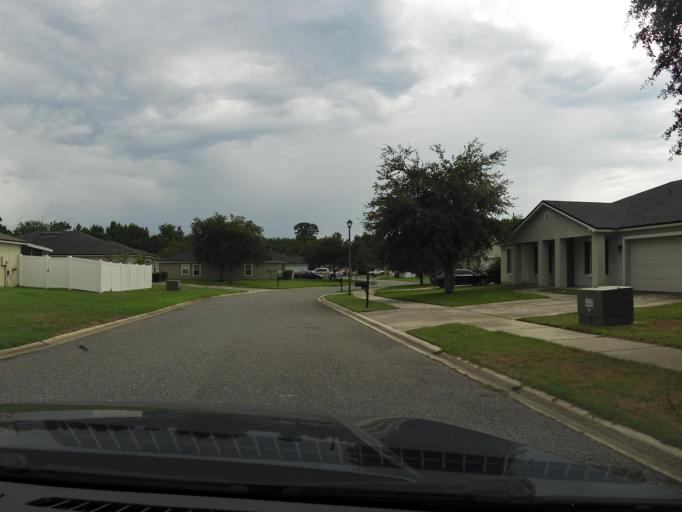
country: US
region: Florida
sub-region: Nassau County
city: Nassau Village-Ratliff
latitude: 30.4445
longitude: -81.7554
